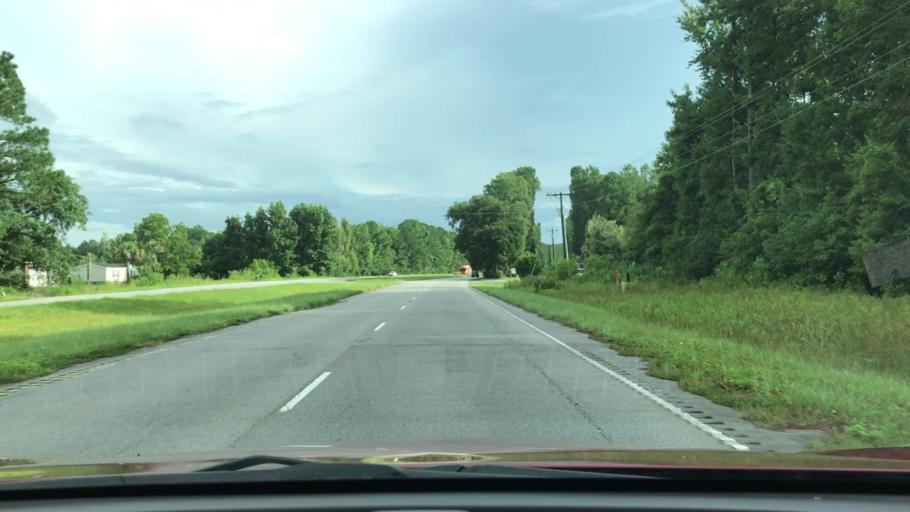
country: US
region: South Carolina
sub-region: Charleston County
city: Awendaw
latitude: 33.0003
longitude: -79.6438
